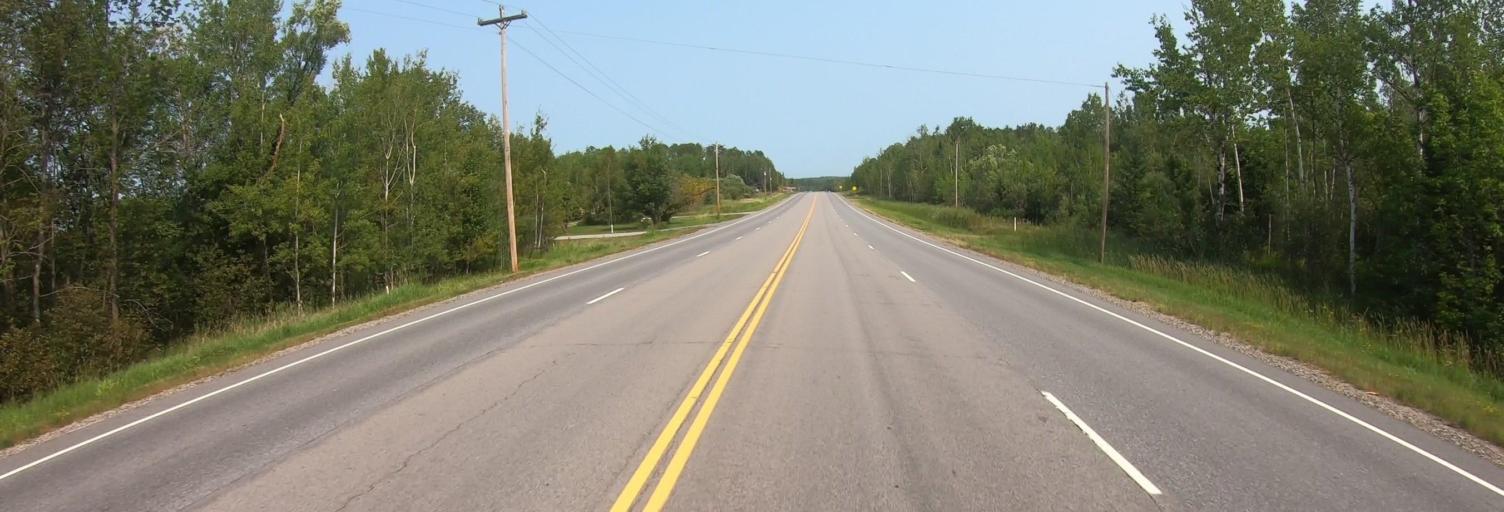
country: US
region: Minnesota
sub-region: Saint Louis County
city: Mountain Iron
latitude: 48.0722
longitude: -92.8227
